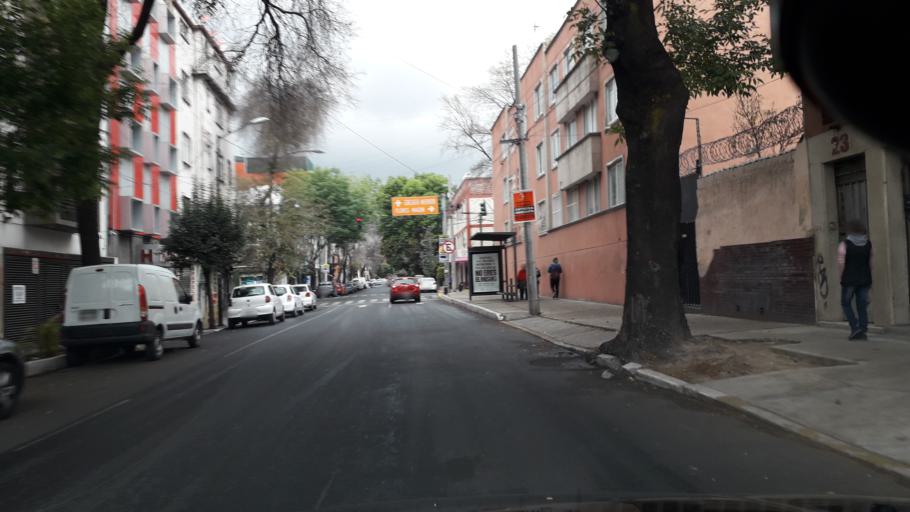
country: MX
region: Mexico City
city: Cuauhtemoc
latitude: 19.4447
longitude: -99.1552
